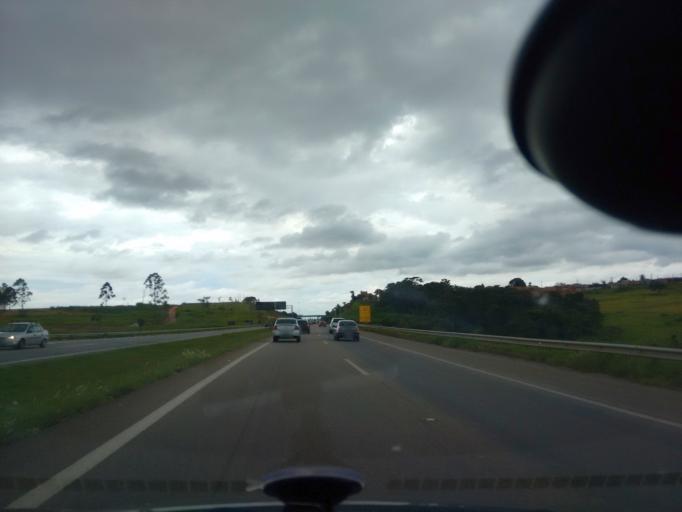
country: BR
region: Sao Paulo
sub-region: Indaiatuba
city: Indaiatuba
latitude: -23.0336
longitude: -47.1331
